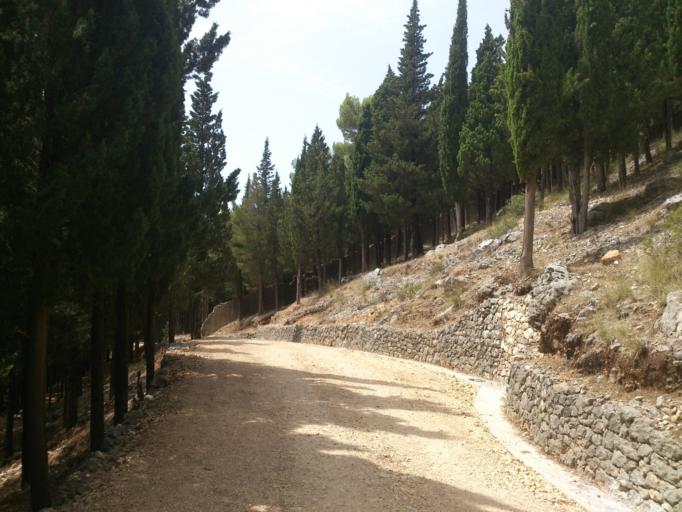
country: IT
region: Calabria
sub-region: Provincia di Reggio Calabria
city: Stilo
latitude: 38.4763
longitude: 16.4617
